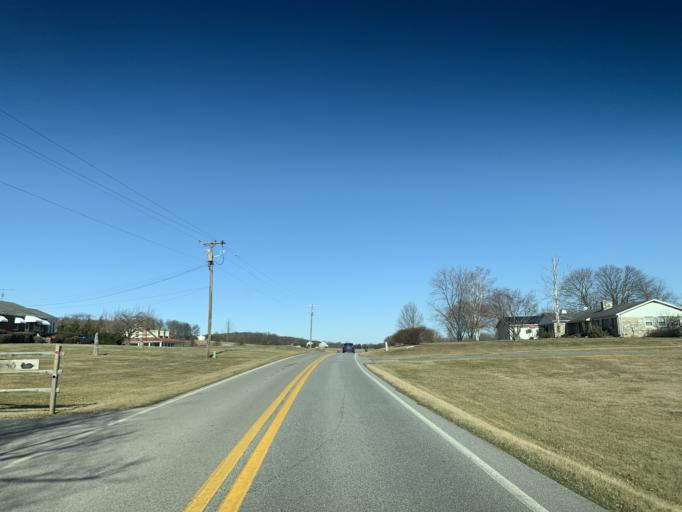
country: US
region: Maryland
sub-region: Carroll County
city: Manchester
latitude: 39.6999
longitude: -76.9008
